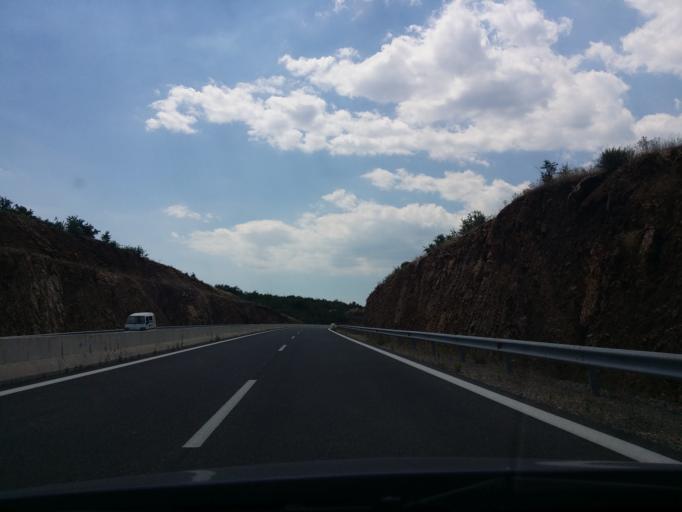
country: GR
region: Peloponnese
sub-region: Nomos Arkadias
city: Megalopoli
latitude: 37.3062
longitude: 22.1890
